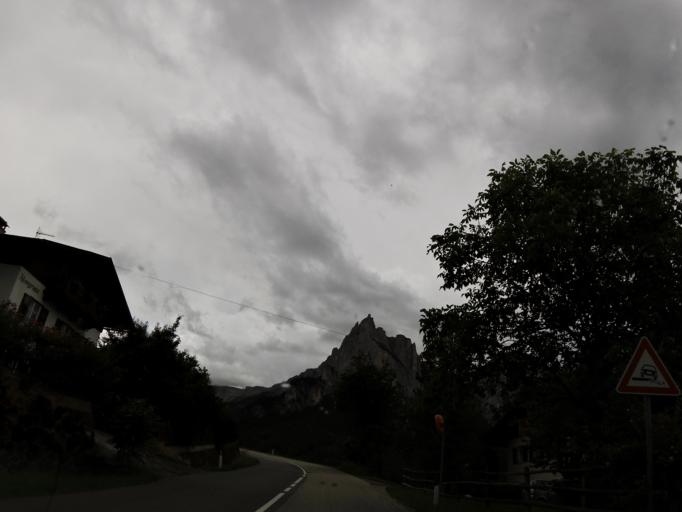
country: IT
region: Trentino-Alto Adige
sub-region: Bolzano
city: Siusi
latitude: 46.5530
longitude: 11.5588
